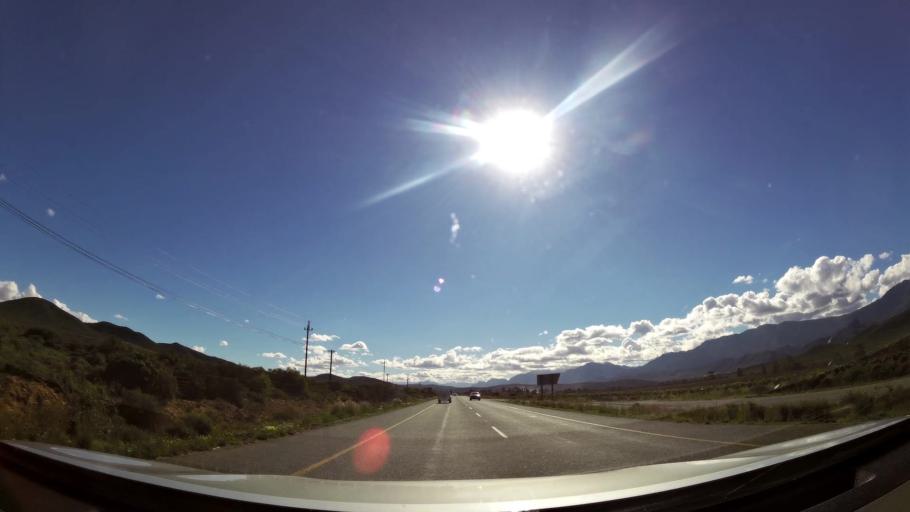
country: ZA
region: Western Cape
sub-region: Cape Winelands District Municipality
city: Ashton
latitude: -33.7720
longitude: 19.7520
